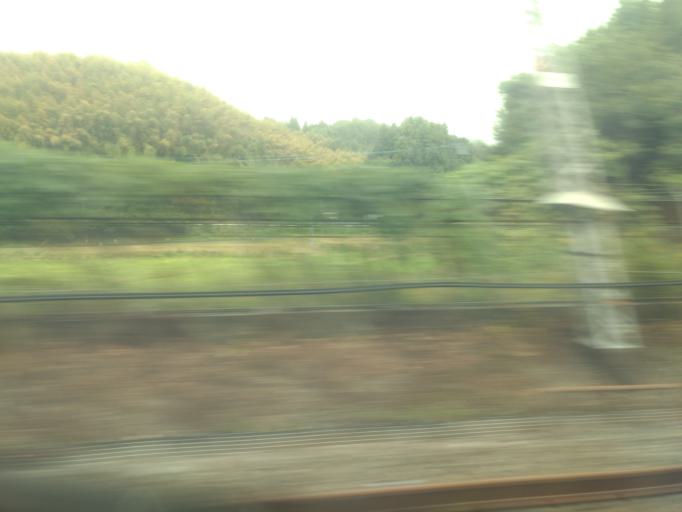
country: JP
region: Yamaguchi
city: Kudamatsu
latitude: 34.0390
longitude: 131.9296
